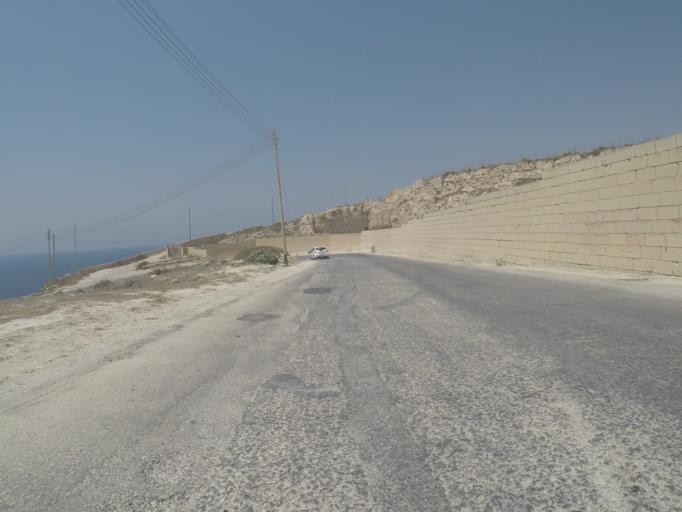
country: MT
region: Is-Siggiewi
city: Siggiewi
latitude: 35.8343
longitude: 14.4173
